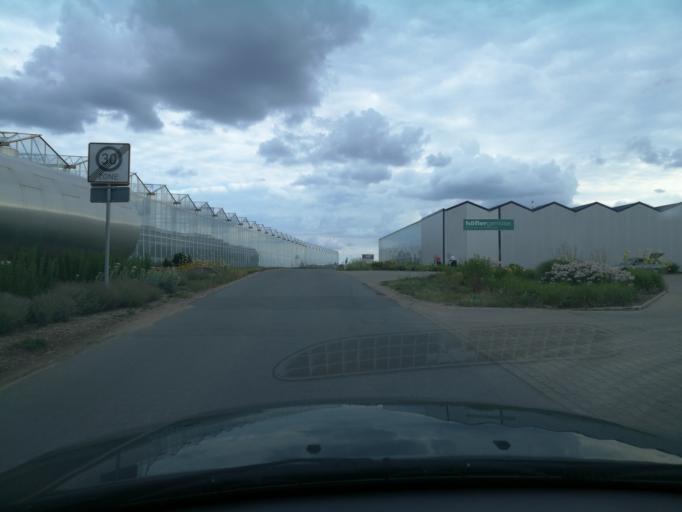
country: DE
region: Bavaria
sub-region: Regierungsbezirk Mittelfranken
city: Wetzendorf
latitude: 49.4837
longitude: 11.0465
